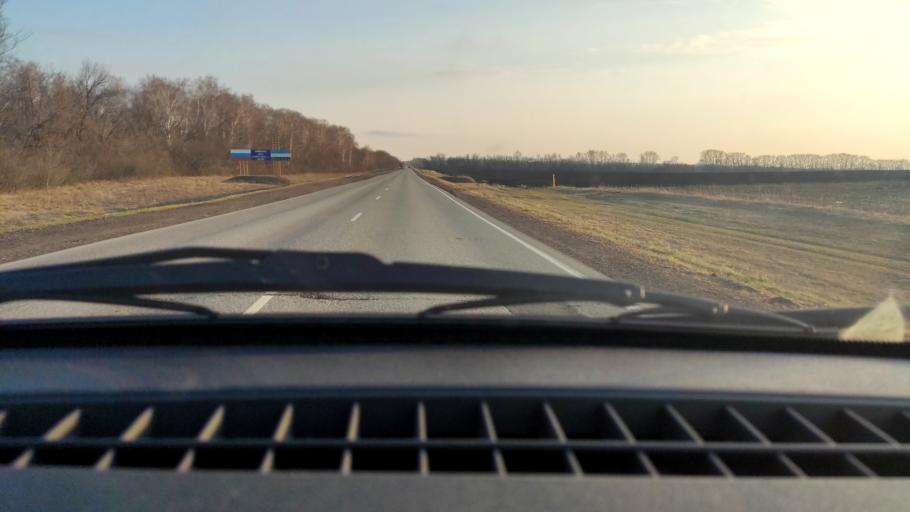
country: RU
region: Bashkortostan
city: Chishmy
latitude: 54.4693
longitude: 55.2611
